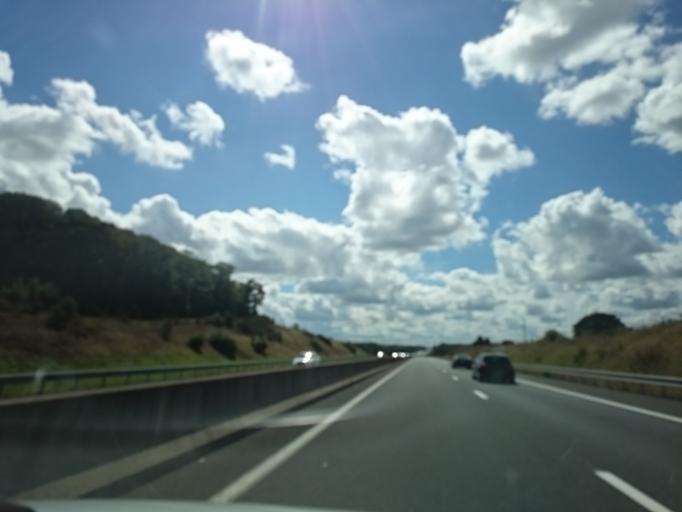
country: FR
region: Pays de la Loire
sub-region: Departement de Maine-et-Loire
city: Saint-Lambert-la-Potherie
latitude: 47.4831
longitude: -0.6639
